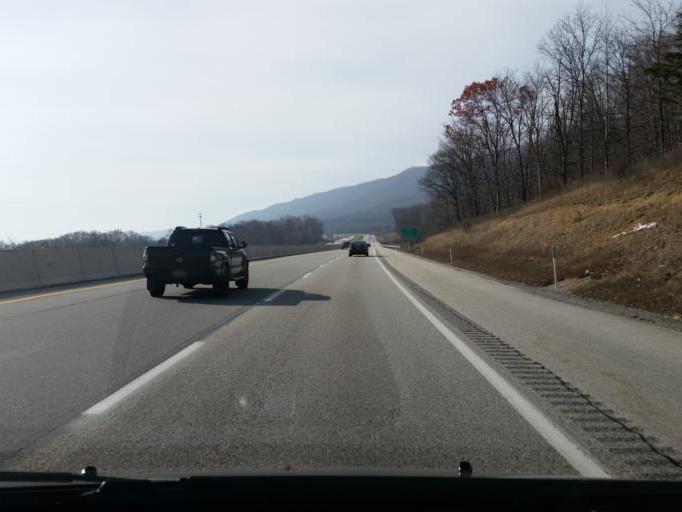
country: US
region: Pennsylvania
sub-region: Franklin County
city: Doylestown
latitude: 40.1536
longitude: -77.6236
